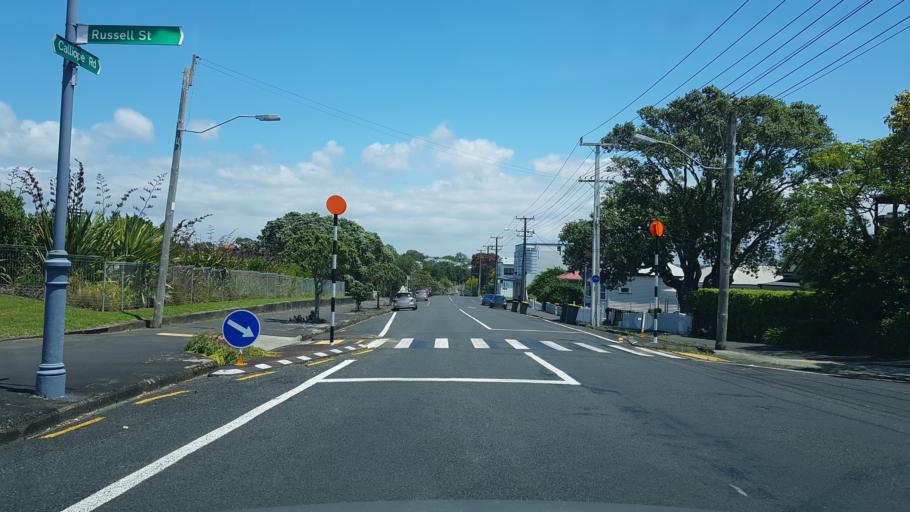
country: NZ
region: Auckland
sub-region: Auckland
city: Auckland
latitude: -36.8276
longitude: 174.7842
